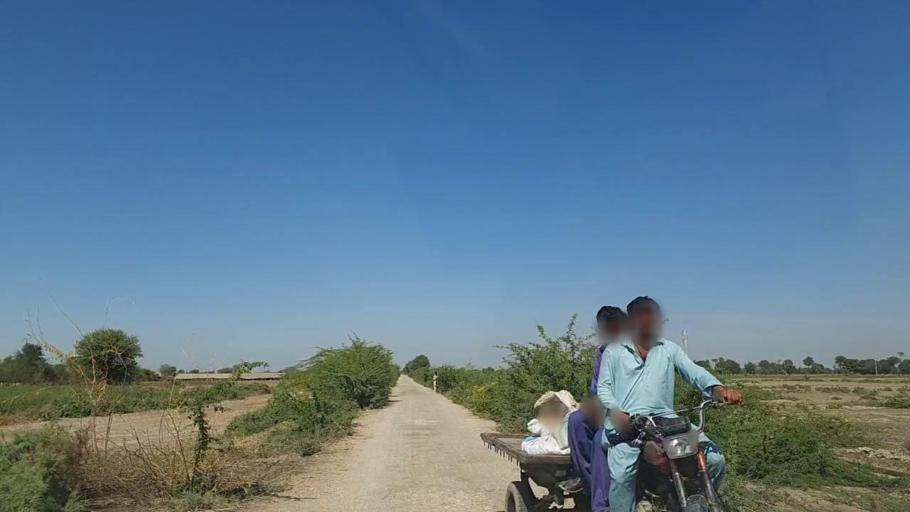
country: PK
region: Sindh
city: Samaro
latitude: 25.2992
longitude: 69.5147
